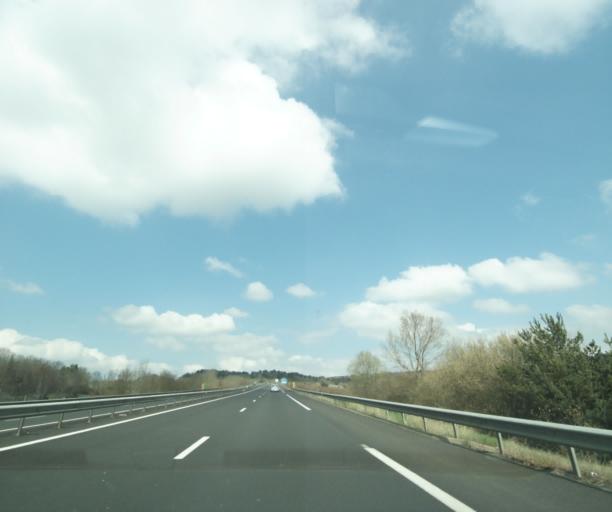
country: FR
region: Auvergne
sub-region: Departement du Cantal
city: Saint-Flour
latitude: 45.0767
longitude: 3.1165
